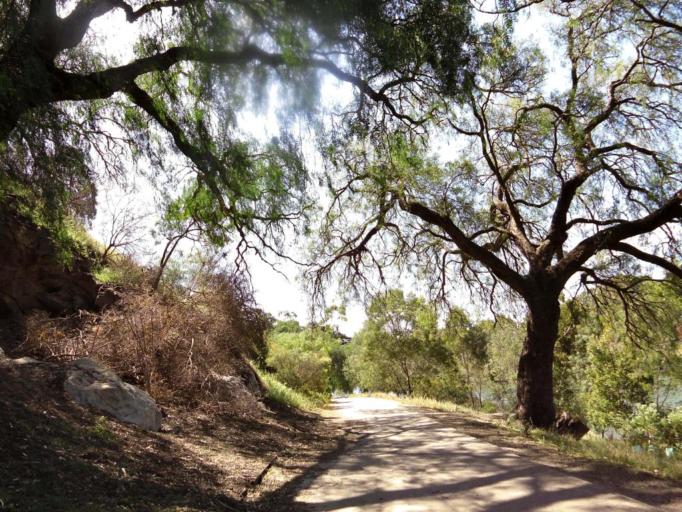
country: AU
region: Victoria
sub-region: Moonee Valley
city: Essendon West
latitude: -37.7648
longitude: 144.8709
